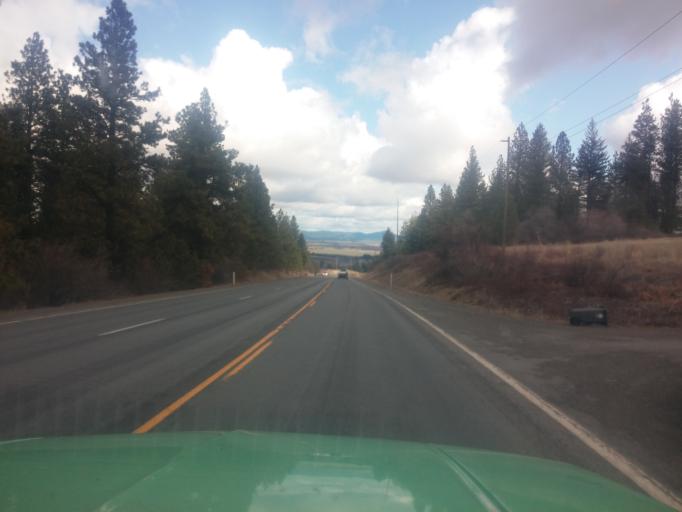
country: US
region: Idaho
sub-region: Latah County
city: Moscow
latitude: 46.8747
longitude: -117.0060
